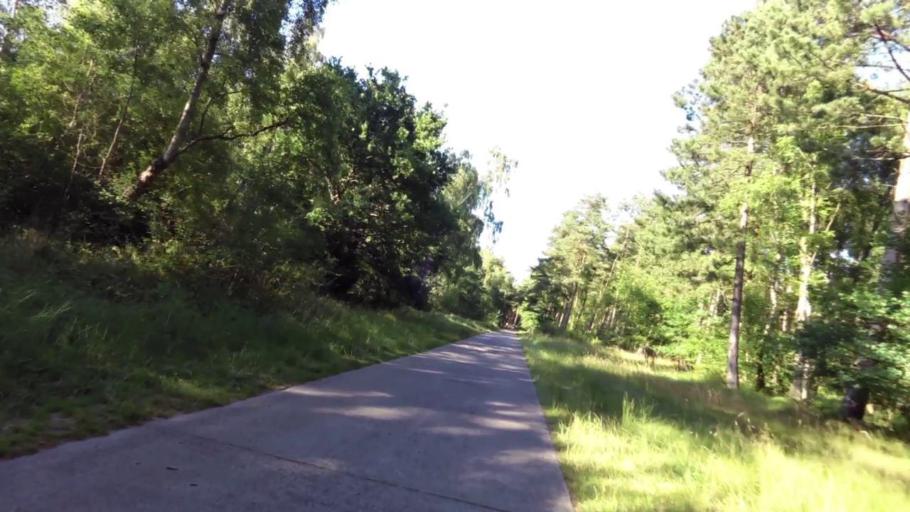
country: PL
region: West Pomeranian Voivodeship
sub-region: Powiat koszalinski
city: Sianow
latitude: 54.3581
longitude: 16.2790
